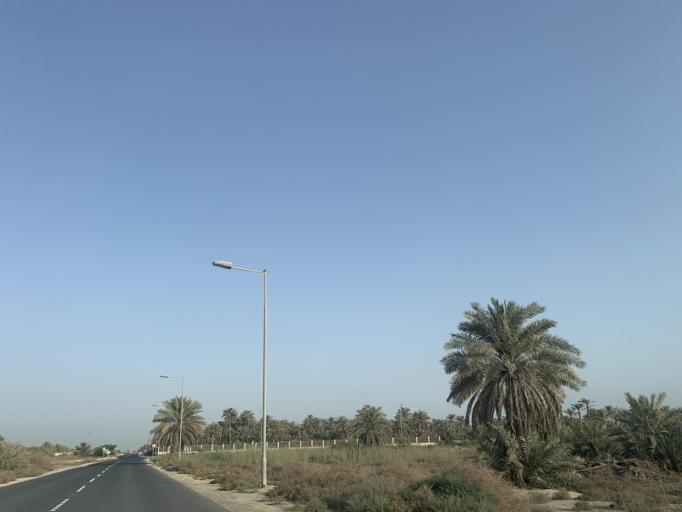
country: BH
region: Central Governorate
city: Madinat Hamad
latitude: 26.1773
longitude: 50.4569
